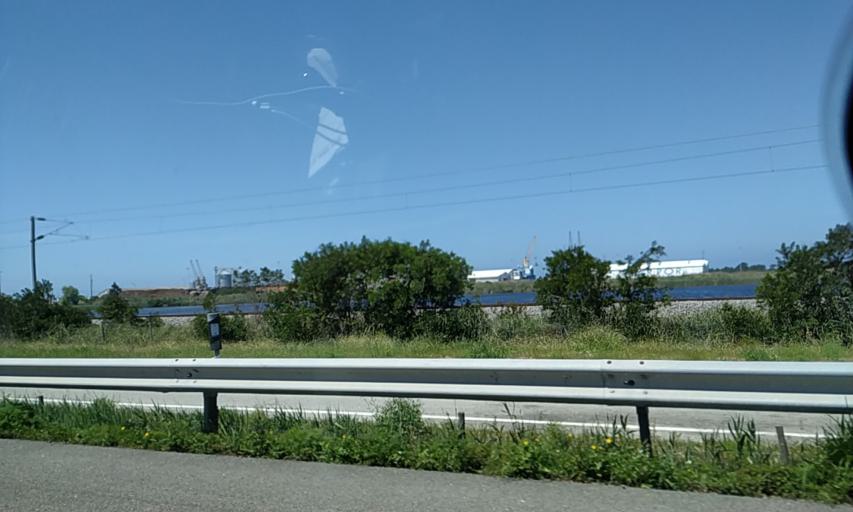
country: PT
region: Aveiro
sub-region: Aveiro
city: Aveiro
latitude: 40.6343
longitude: -8.6769
